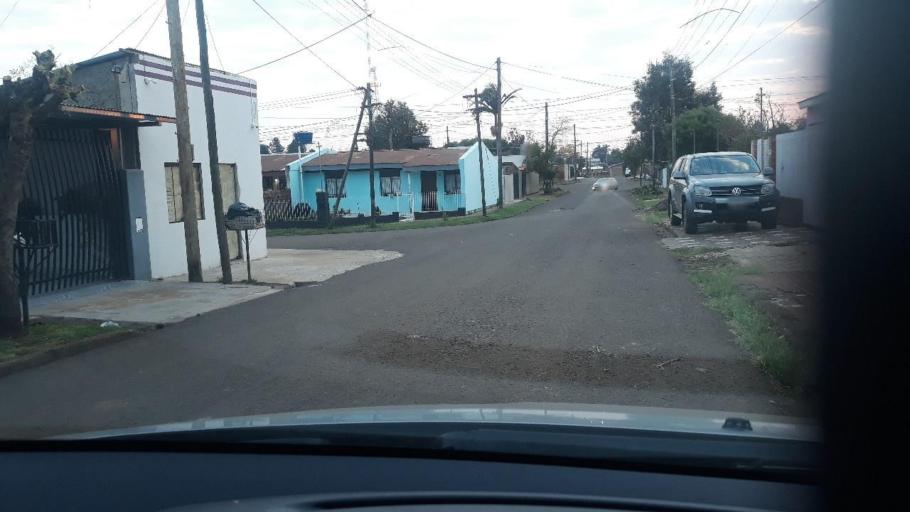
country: AR
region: Misiones
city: Bernardo de Irigoyen
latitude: -26.2516
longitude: -53.6519
